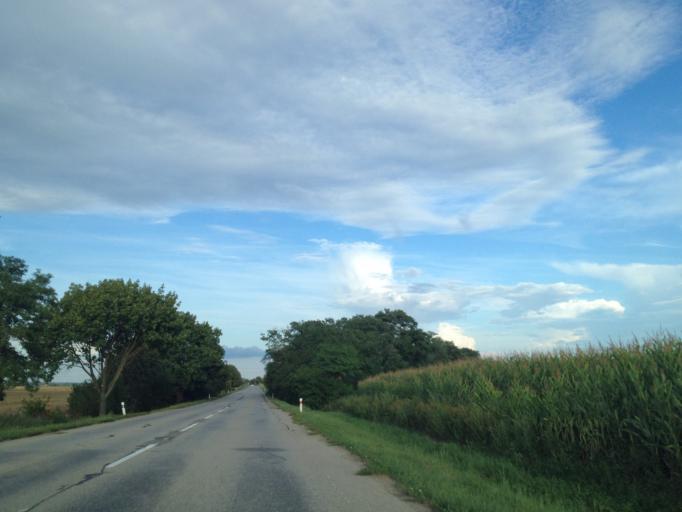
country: SK
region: Nitriansky
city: Svodin
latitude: 47.8995
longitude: 18.3638
